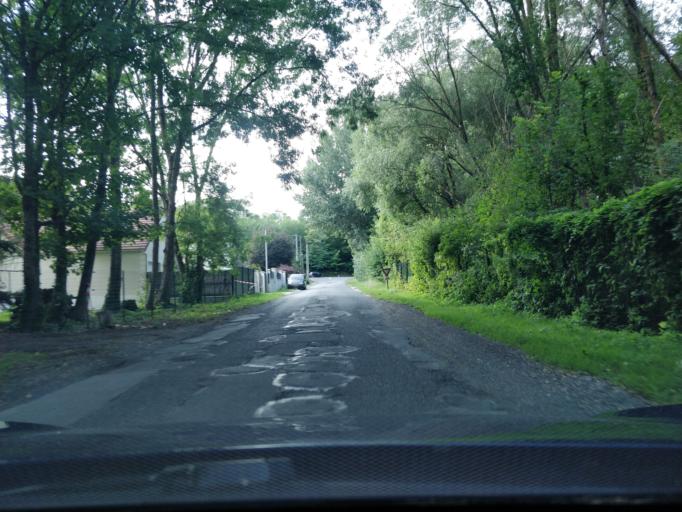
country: FR
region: Ile-de-France
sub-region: Departement de l'Essonne
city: Etampes
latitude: 48.4157
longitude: 2.1497
